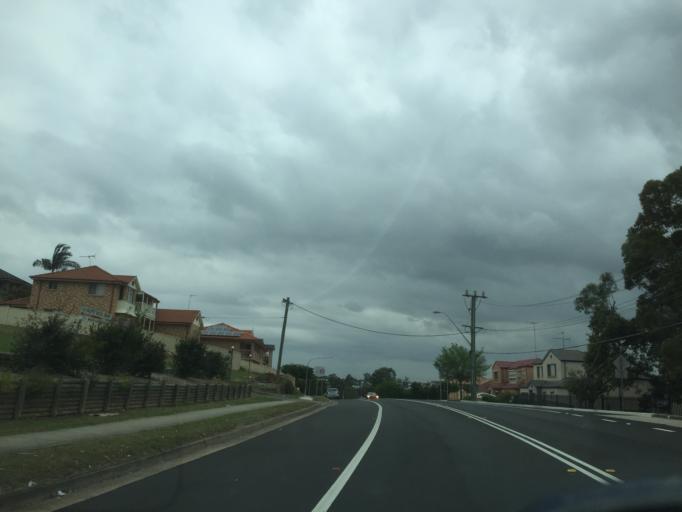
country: AU
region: New South Wales
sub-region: Blacktown
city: Doonside
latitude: -33.7875
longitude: 150.8911
